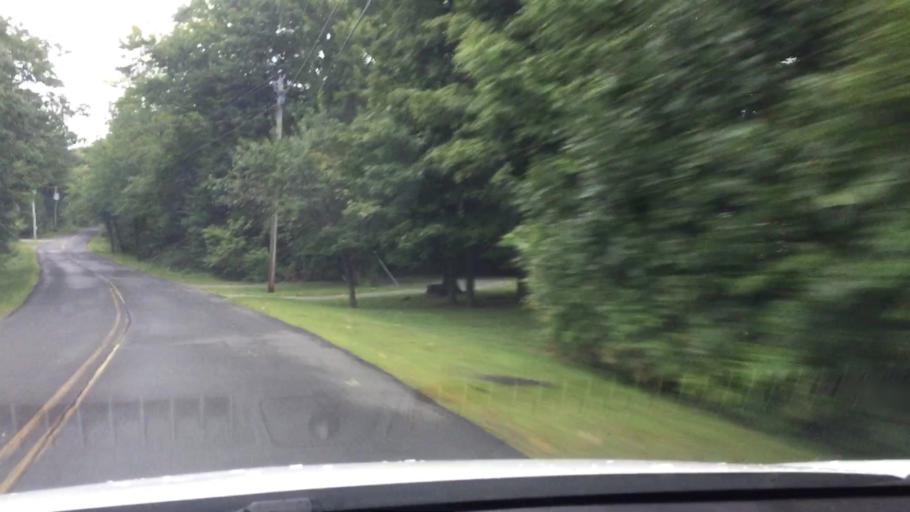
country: US
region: Massachusetts
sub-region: Berkshire County
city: Otis
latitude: 42.1668
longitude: -73.0543
